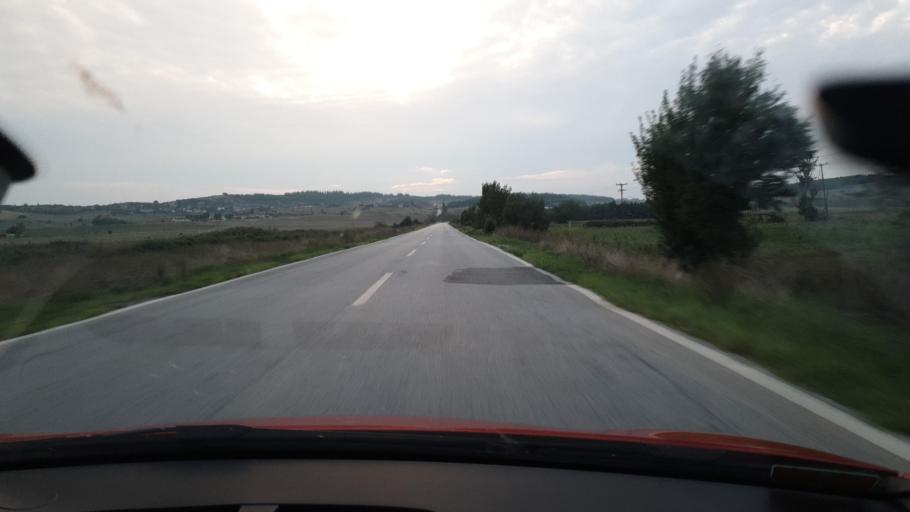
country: GR
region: Central Macedonia
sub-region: Nomos Kilkis
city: Kristoni
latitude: 40.9951
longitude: 22.7489
